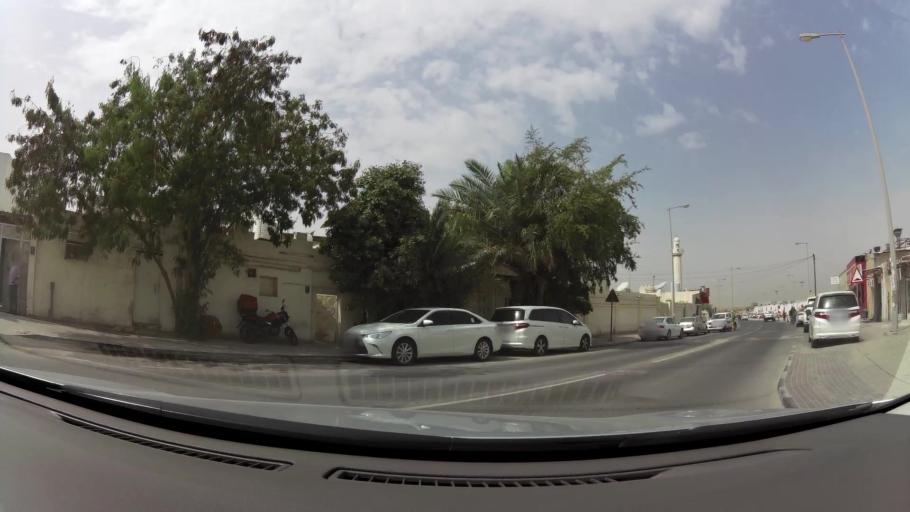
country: QA
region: Baladiyat ad Dawhah
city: Doha
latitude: 25.3019
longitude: 51.4934
